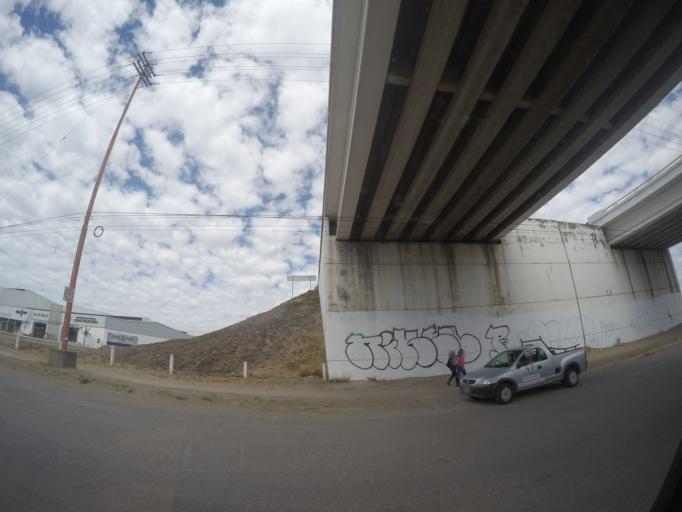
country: MX
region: Guanajuato
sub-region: Leon
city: San Jose de Duran (Los Troncoso)
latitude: 21.0720
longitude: -101.6831
